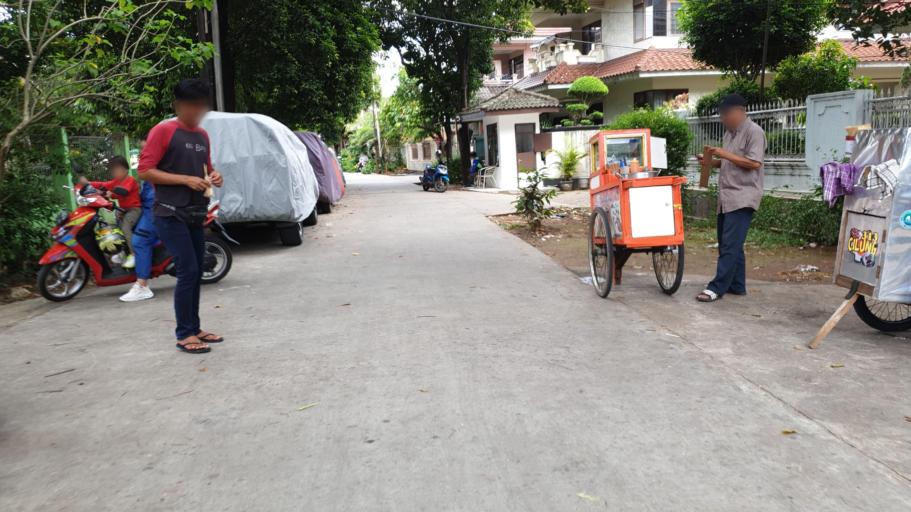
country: ID
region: Jakarta Raya
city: Jakarta
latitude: -6.2661
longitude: 106.7911
